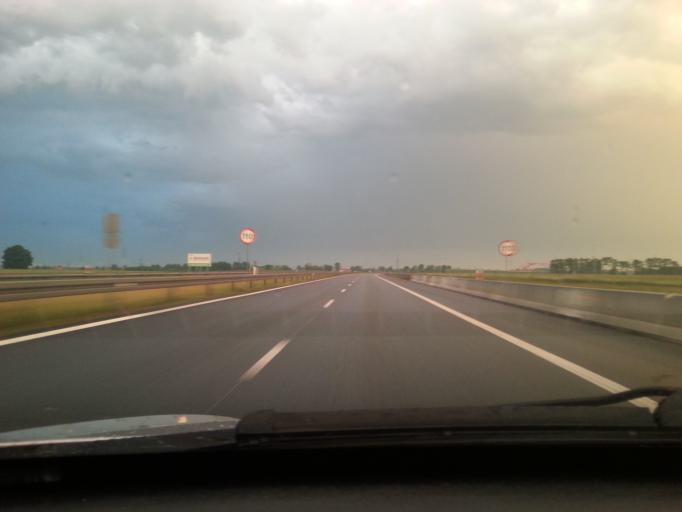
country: PL
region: Lodz Voivodeship
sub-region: Powiat pabianicki
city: Pabianice
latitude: 51.6950
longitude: 19.3414
